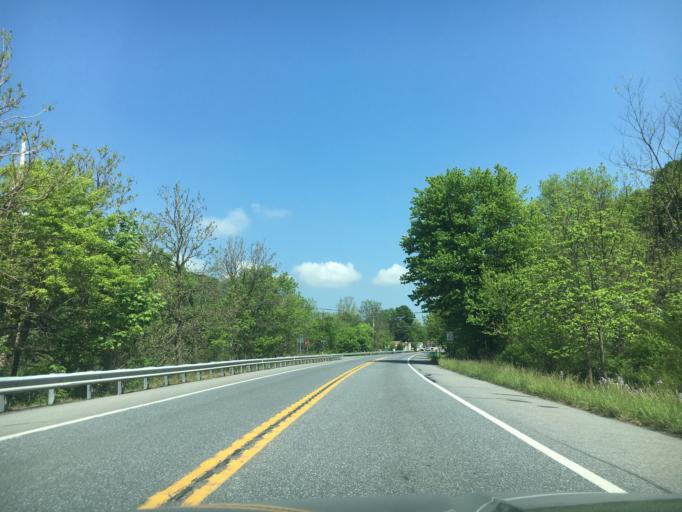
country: US
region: Pennsylvania
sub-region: Berks County
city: Boyertown
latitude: 40.3395
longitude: -75.6579
